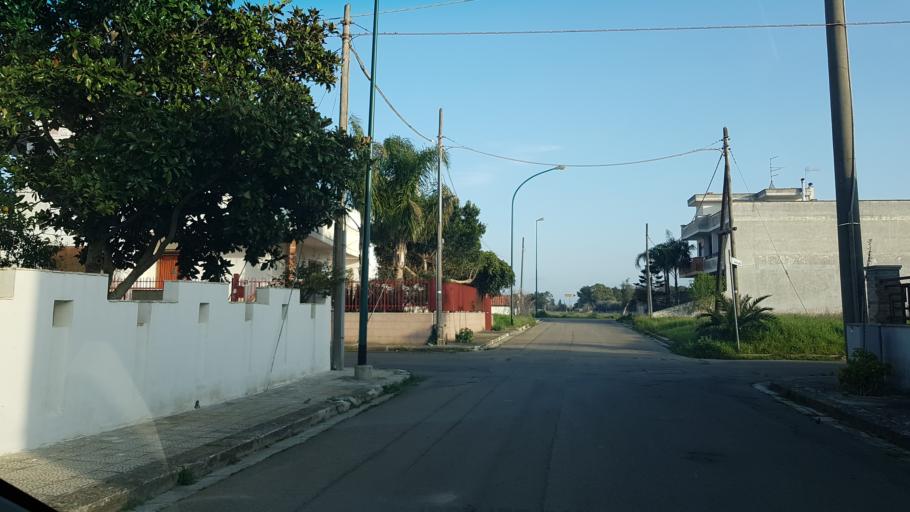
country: IT
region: Apulia
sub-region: Provincia di Lecce
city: Campi Salentina
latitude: 40.3931
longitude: 18.0237
